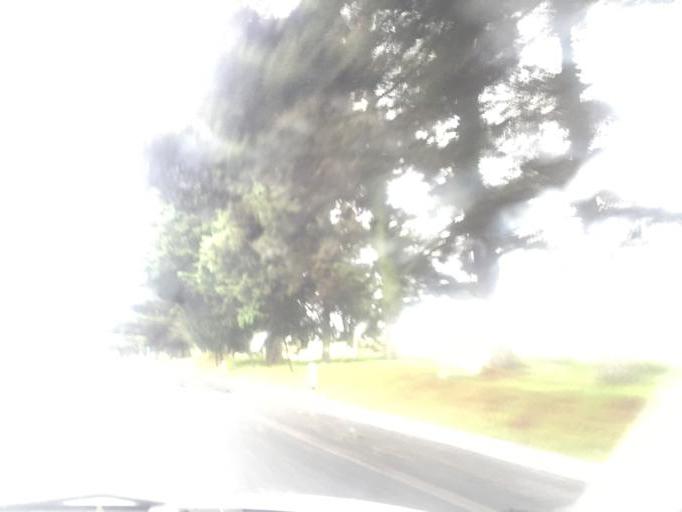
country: MX
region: Mexico City
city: Xochimilco
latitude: 19.1755
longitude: -99.1529
